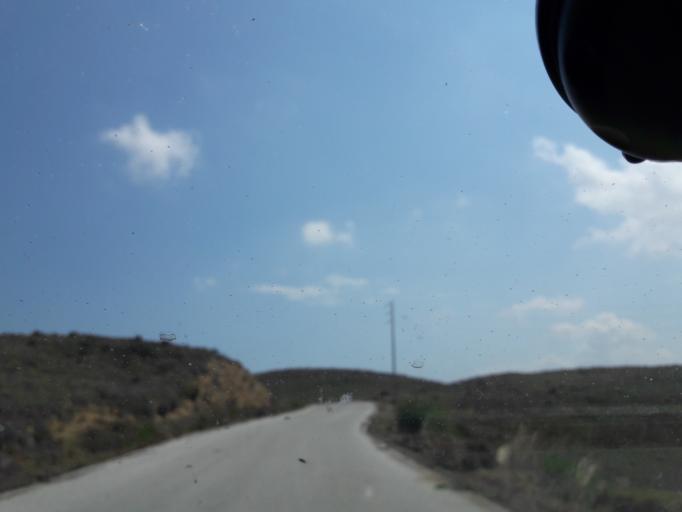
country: GR
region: North Aegean
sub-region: Nomos Lesvou
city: Myrina
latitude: 39.9766
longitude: 25.3507
